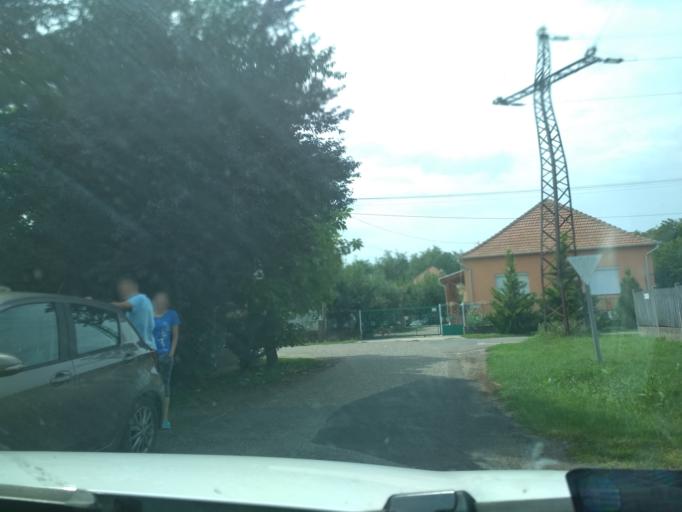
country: HU
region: Jasz-Nagykun-Szolnok
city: Tiszafured
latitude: 47.6098
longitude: 20.7668
